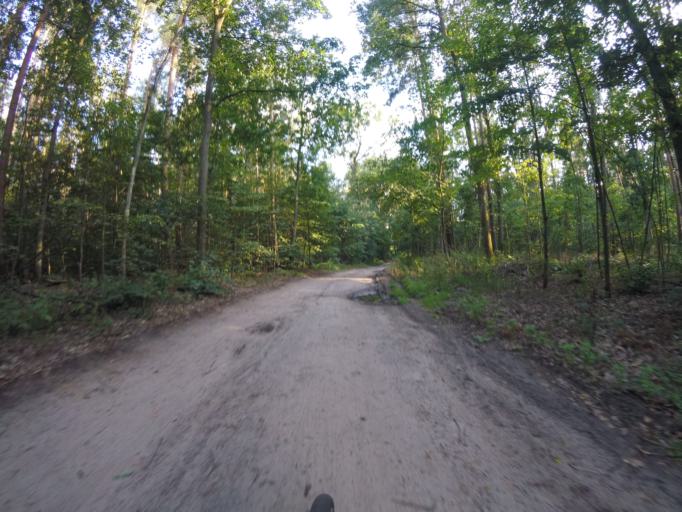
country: DE
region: Brandenburg
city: Petershagen
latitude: 52.5682
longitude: 13.8234
